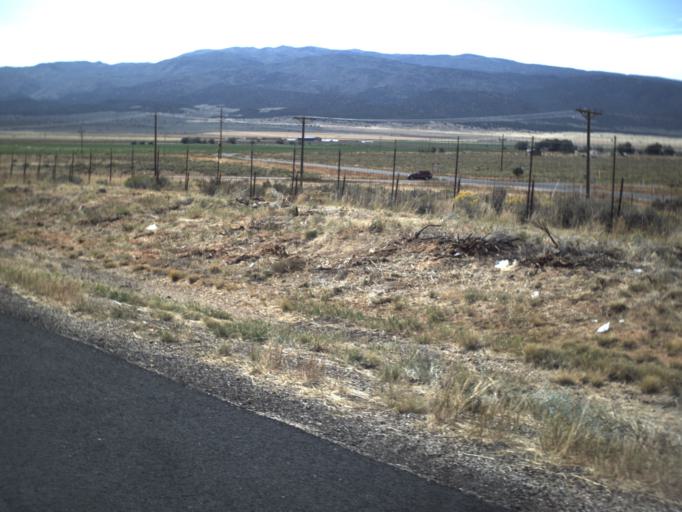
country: US
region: Utah
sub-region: Iron County
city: Cedar City
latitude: 37.6047
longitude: -113.1602
